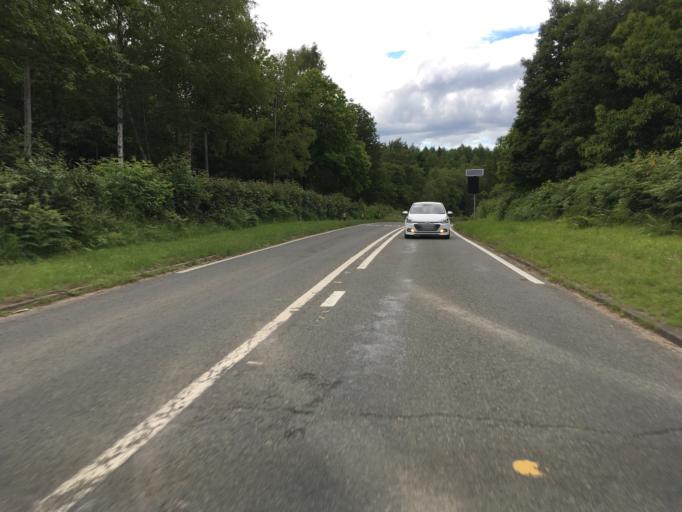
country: GB
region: England
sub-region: Oxfordshire
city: Boars Hill
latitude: 51.7148
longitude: -1.2663
